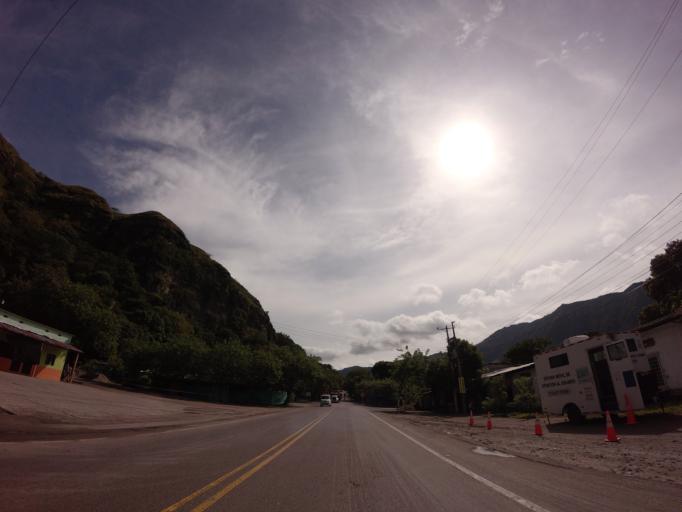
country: CO
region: Tolima
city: Honda
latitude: 5.2307
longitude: -74.7327
